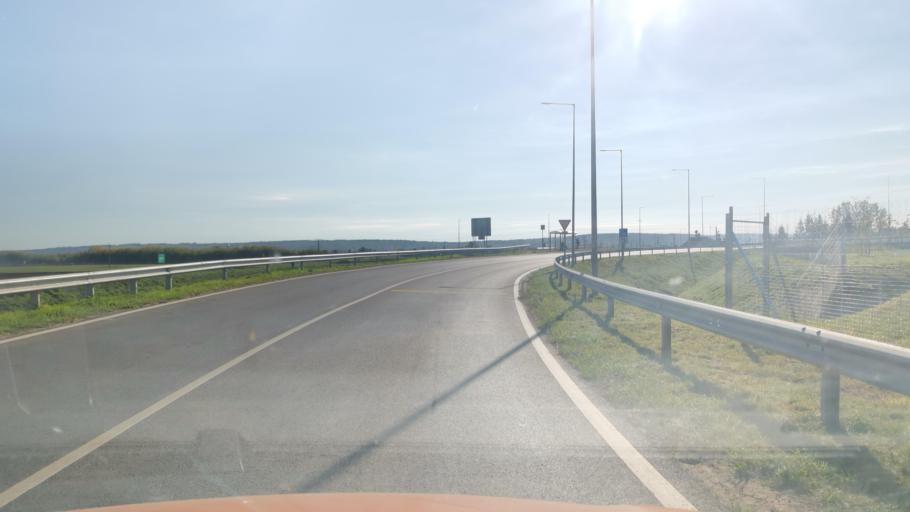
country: HU
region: Borsod-Abauj-Zemplen
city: Halmaj
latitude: 48.2543
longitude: 20.9797
